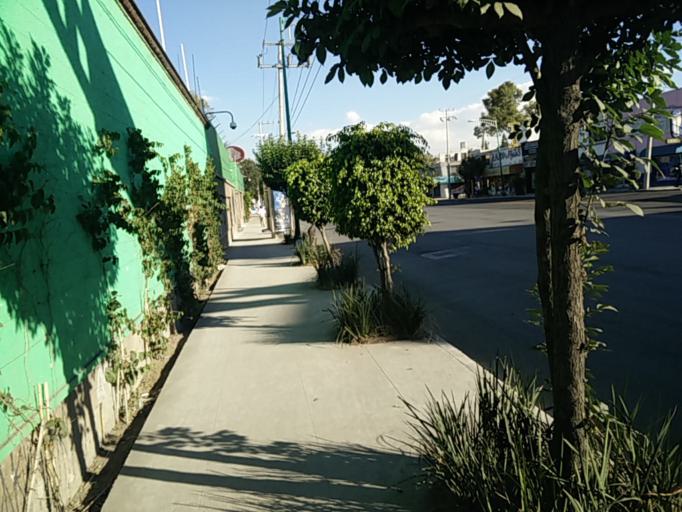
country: MX
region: Mexico
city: Colonia Lindavista
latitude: 19.4896
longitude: -99.1297
